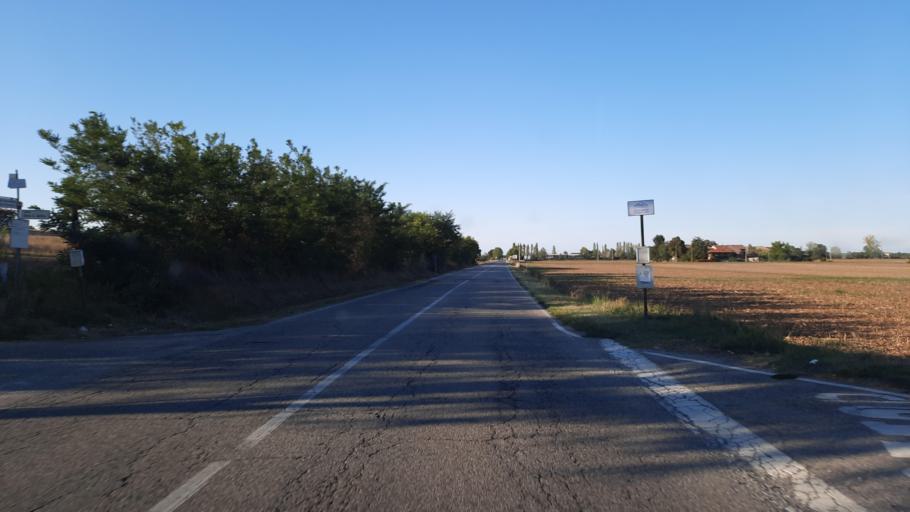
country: IT
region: Piedmont
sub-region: Provincia di Alessandria
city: Terruggia
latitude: 45.0679
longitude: 8.4678
